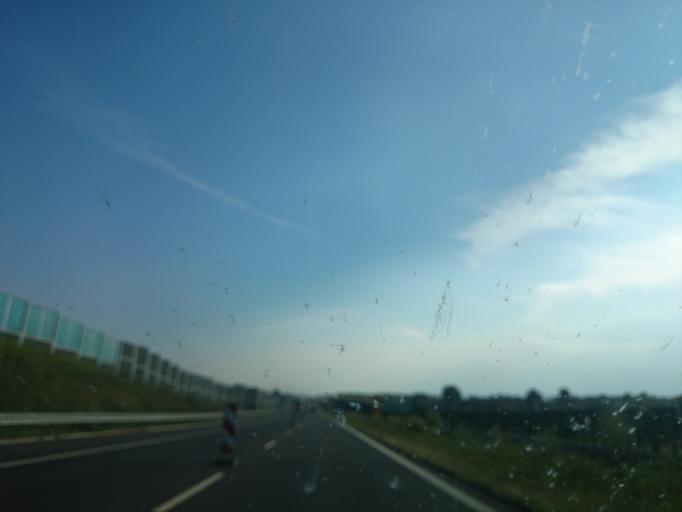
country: PL
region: Silesian Voivodeship
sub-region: Powiat rybnicki
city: Swierklany Dolne
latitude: 50.0074
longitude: 18.5822
